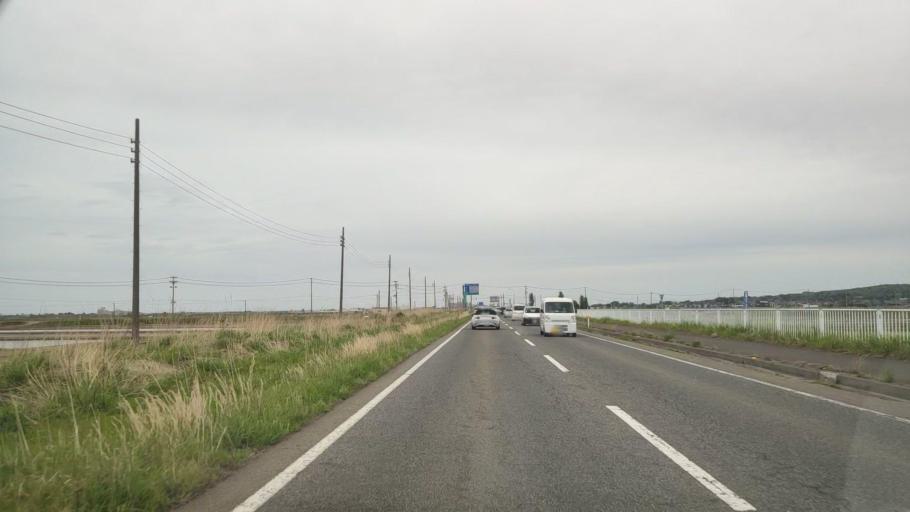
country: JP
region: Niigata
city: Niitsu-honcho
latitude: 37.7688
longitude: 139.1010
